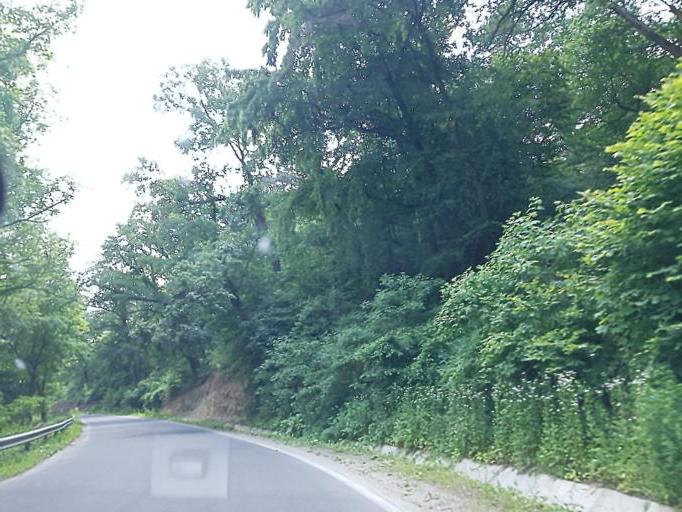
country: RO
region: Sibiu
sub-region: Comuna Seica Mare
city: Seica Mare
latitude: 46.0357
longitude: 24.1594
